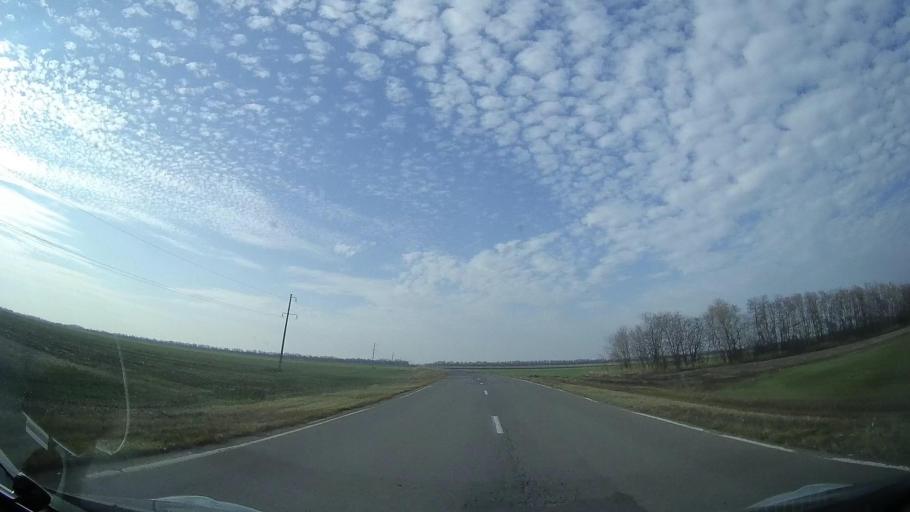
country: RU
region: Rostov
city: Veselyy
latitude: 46.9692
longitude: 40.6807
